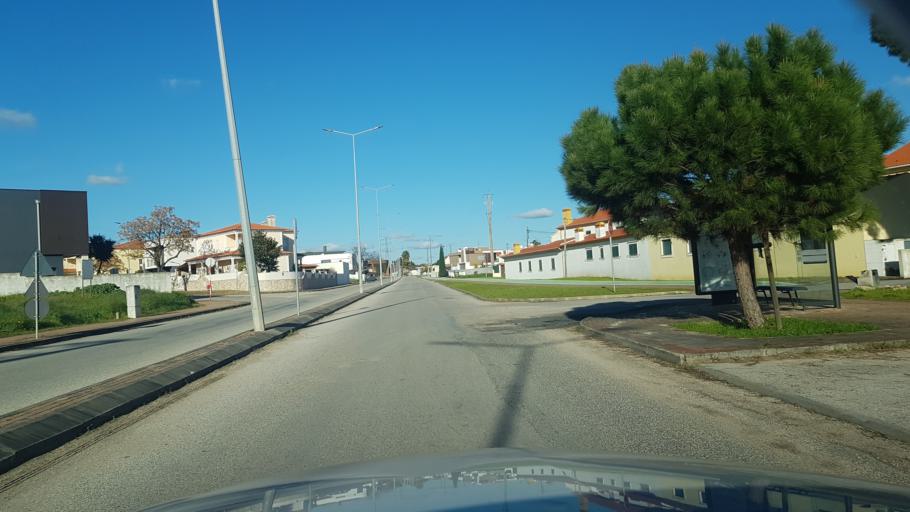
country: PT
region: Santarem
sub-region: Entroncamento
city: Entroncamento
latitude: 39.4788
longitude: -8.4734
